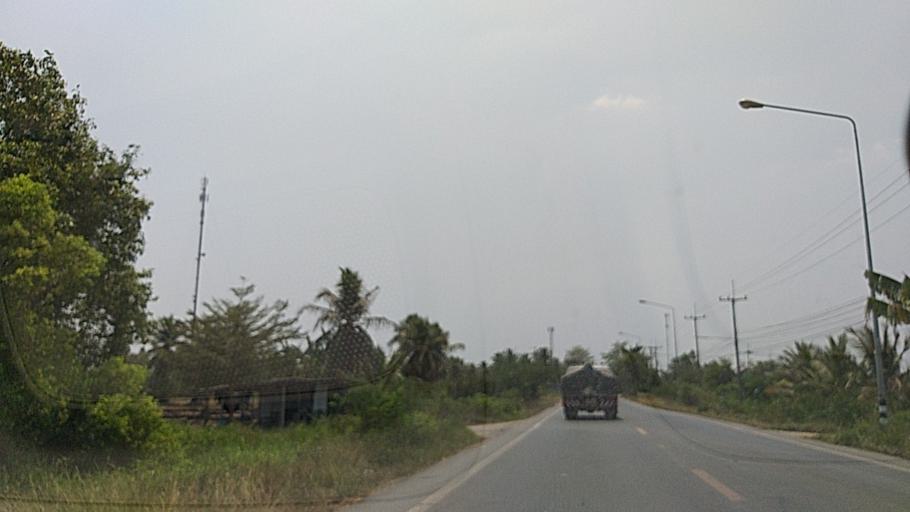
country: TH
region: Chachoengsao
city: Bang Nam Priao
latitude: 13.9268
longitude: 100.9765
